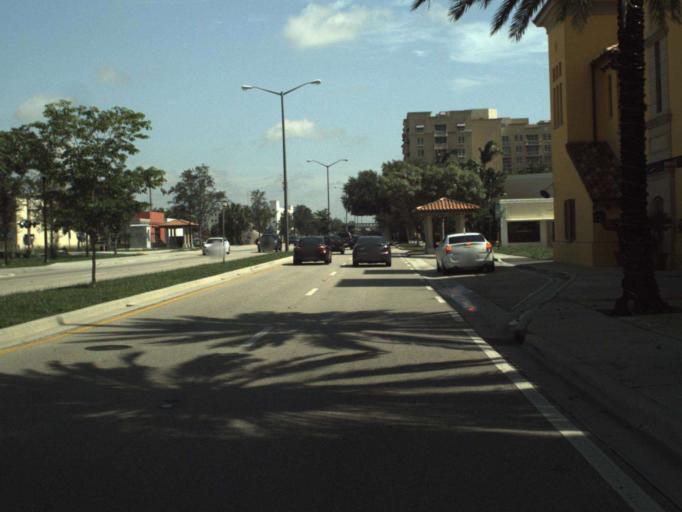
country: US
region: Florida
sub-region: Palm Beach County
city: West Palm Beach
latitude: 26.7087
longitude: -80.0550
